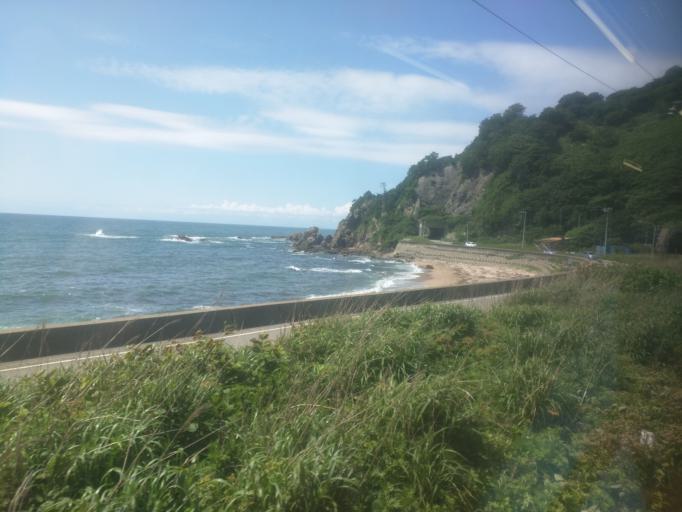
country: JP
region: Niigata
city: Murakami
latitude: 38.4149
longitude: 139.4688
